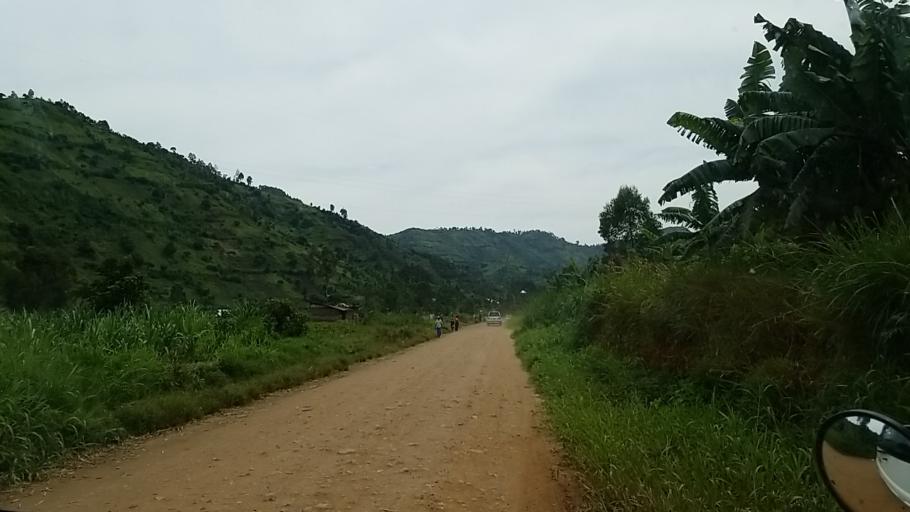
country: CD
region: Nord Kivu
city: Sake
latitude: -1.7237
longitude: 29.0112
